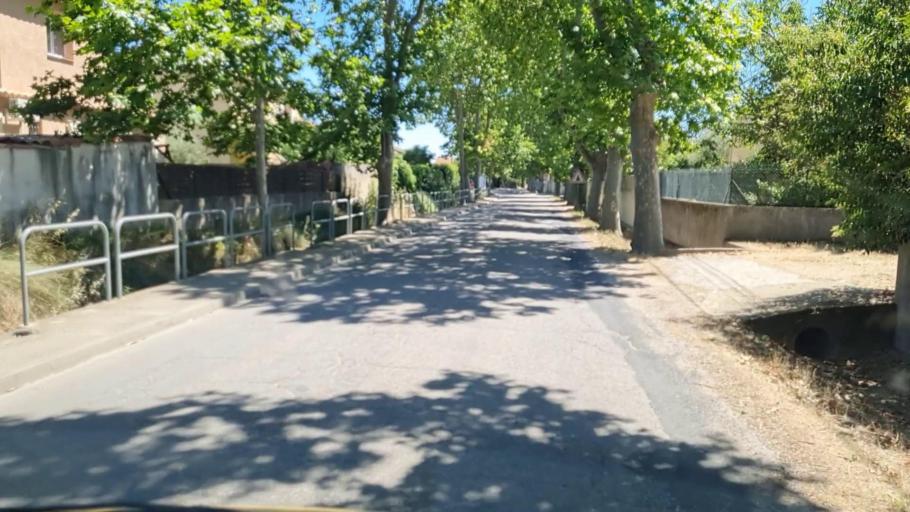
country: FR
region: Languedoc-Roussillon
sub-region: Departement du Gard
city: Le Cailar
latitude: 43.6813
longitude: 4.2347
